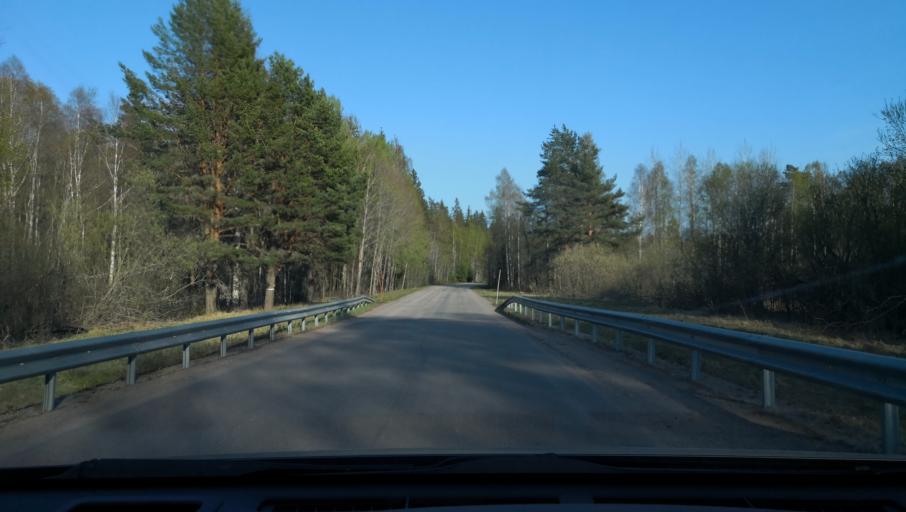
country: SE
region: Uppsala
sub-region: Heby Kommun
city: Tarnsjo
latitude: 60.2658
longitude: 16.9200
